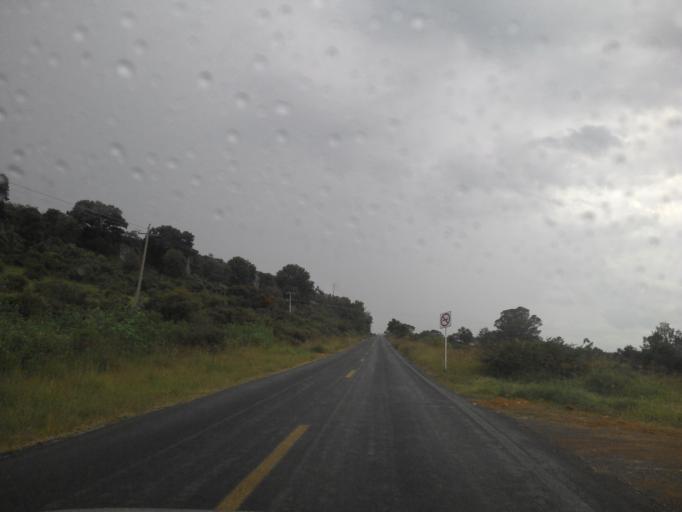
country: MX
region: Jalisco
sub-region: Arandas
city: Santiaguito (Santiaguito de Velazquez)
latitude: 20.7945
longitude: -102.2519
